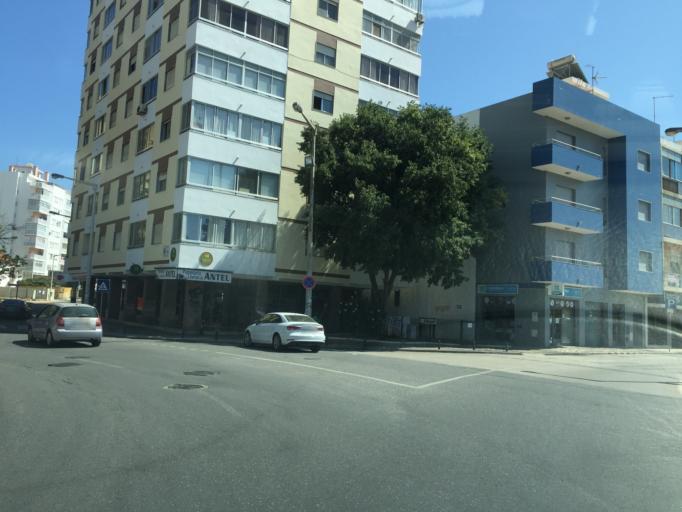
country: PT
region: Faro
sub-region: Faro
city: Faro
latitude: 37.0242
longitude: -7.9267
